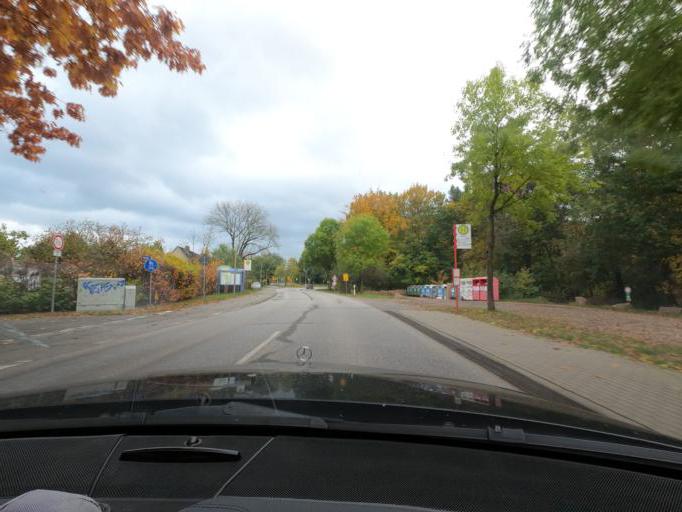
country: DE
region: Schleswig-Holstein
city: Geesthacht
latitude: 53.4471
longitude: 10.3734
